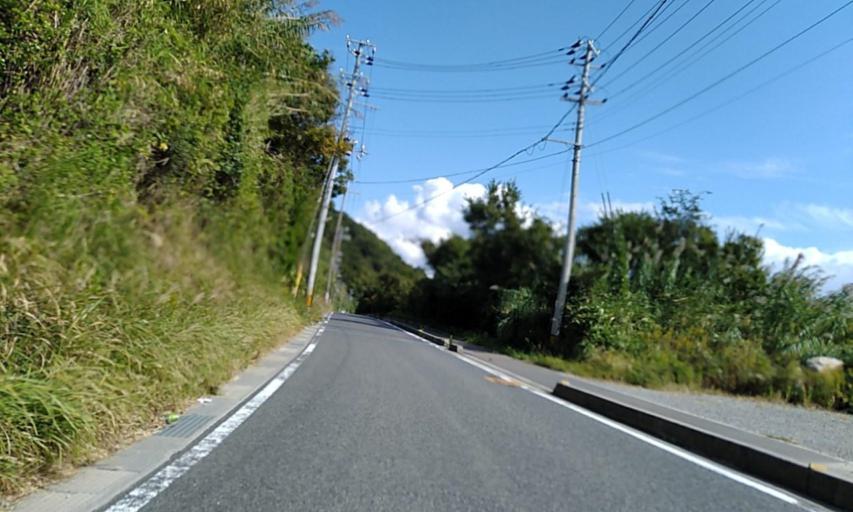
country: JP
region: Wakayama
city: Gobo
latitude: 33.9639
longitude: 135.1026
